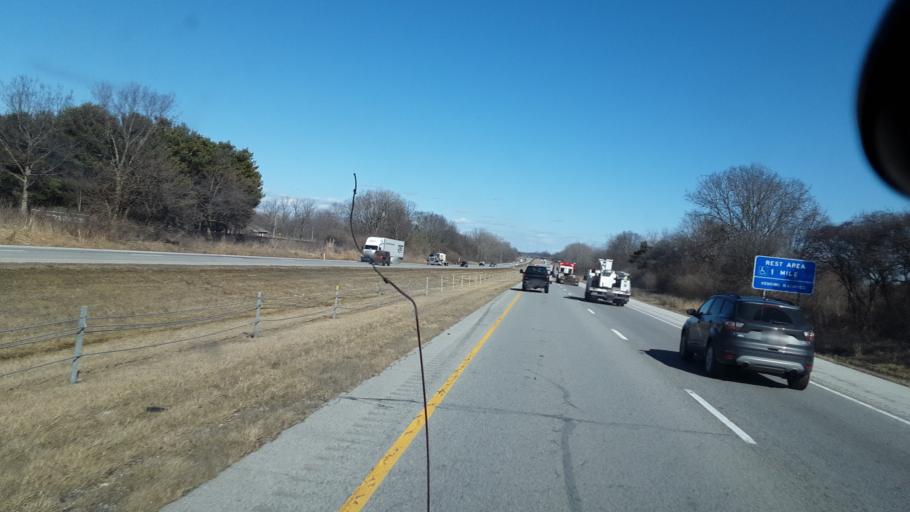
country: US
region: Indiana
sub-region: Morgan County
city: Mooresville
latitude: 39.6431
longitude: -86.4204
